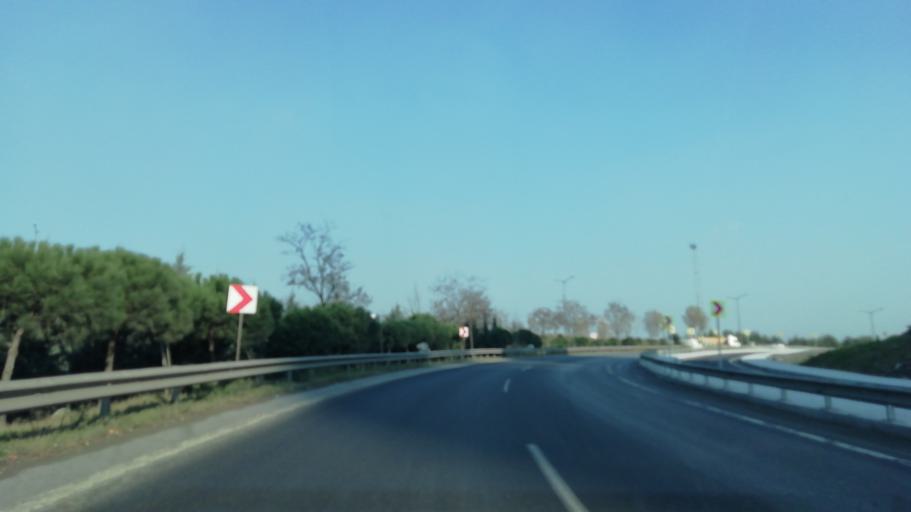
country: TR
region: Istanbul
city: Sultangazi
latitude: 41.0897
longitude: 28.9075
